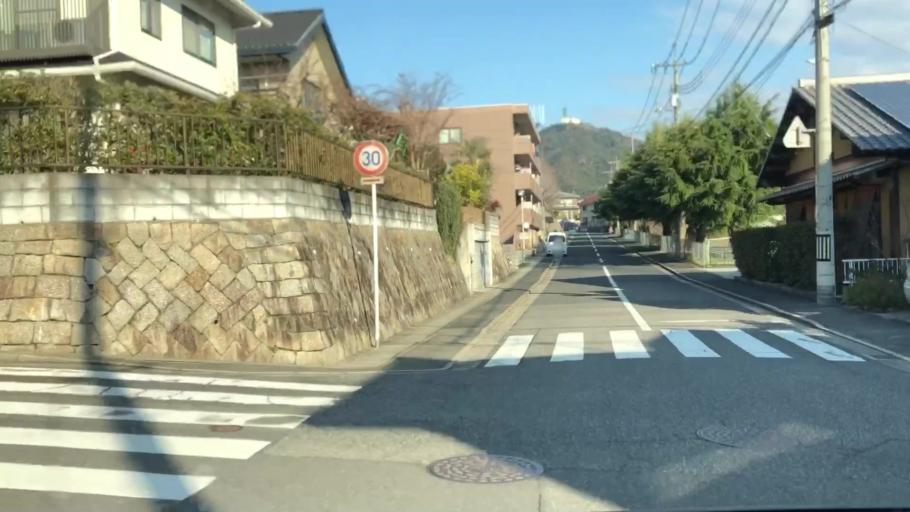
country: JP
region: Hiroshima
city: Hiroshima-shi
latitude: 34.4024
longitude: 132.4135
